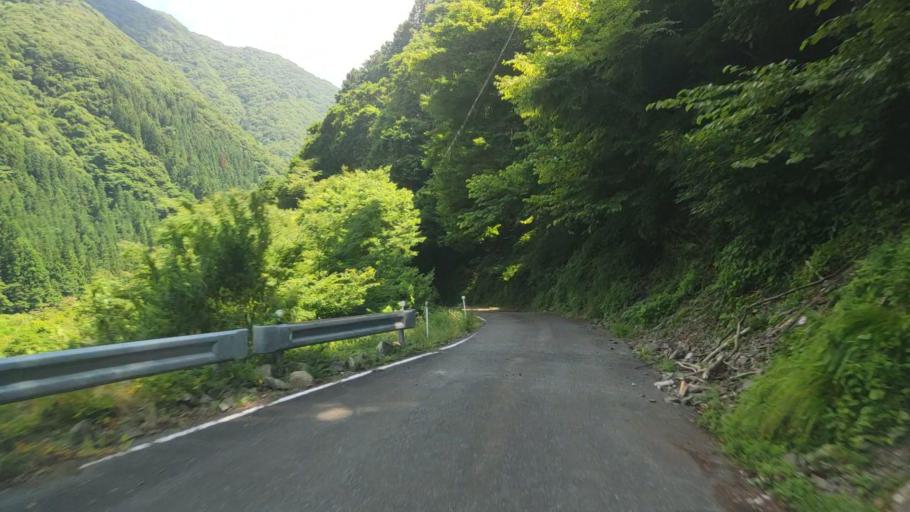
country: JP
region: Gifu
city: Godo
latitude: 35.6980
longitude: 136.5920
